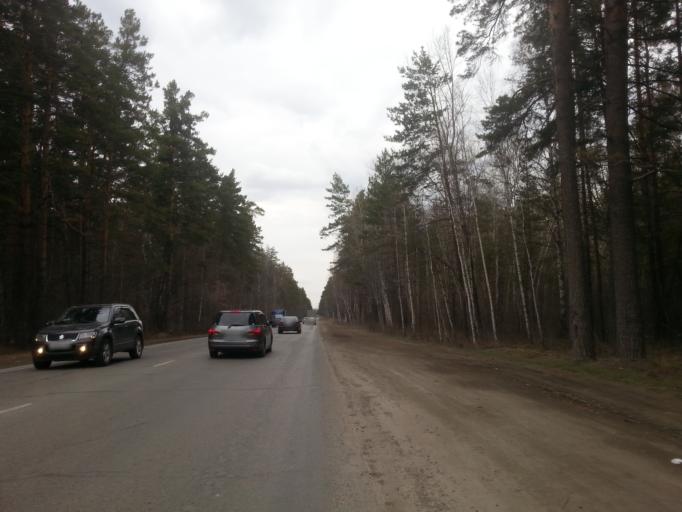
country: RU
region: Altai Krai
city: Yuzhnyy
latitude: 53.2754
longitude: 83.7209
